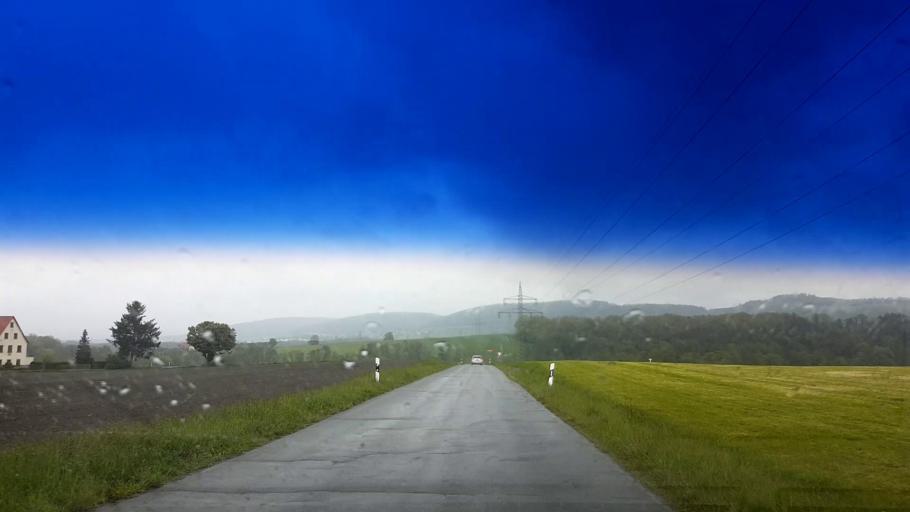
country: DE
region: Bavaria
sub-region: Upper Franconia
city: Gesees
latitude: 50.0282
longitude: 11.6280
